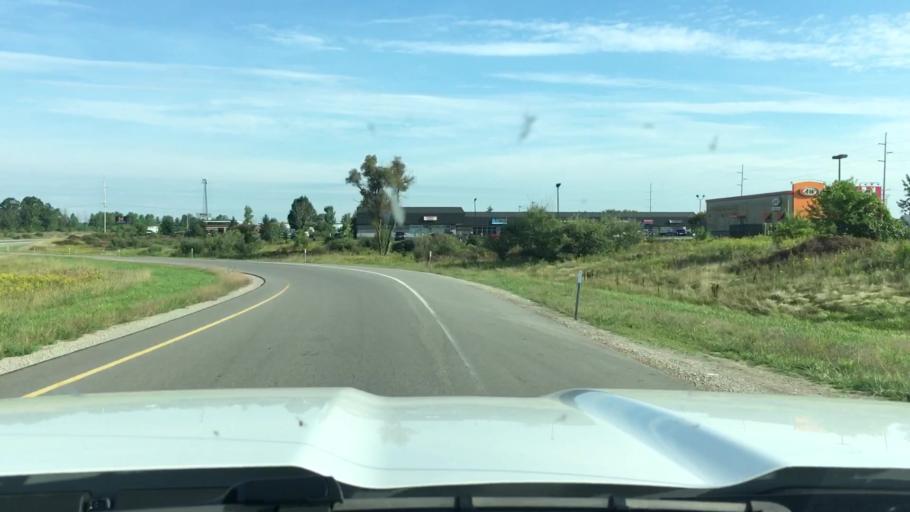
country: US
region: Michigan
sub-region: Kent County
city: Cedar Springs
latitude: 43.2203
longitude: -85.5724
